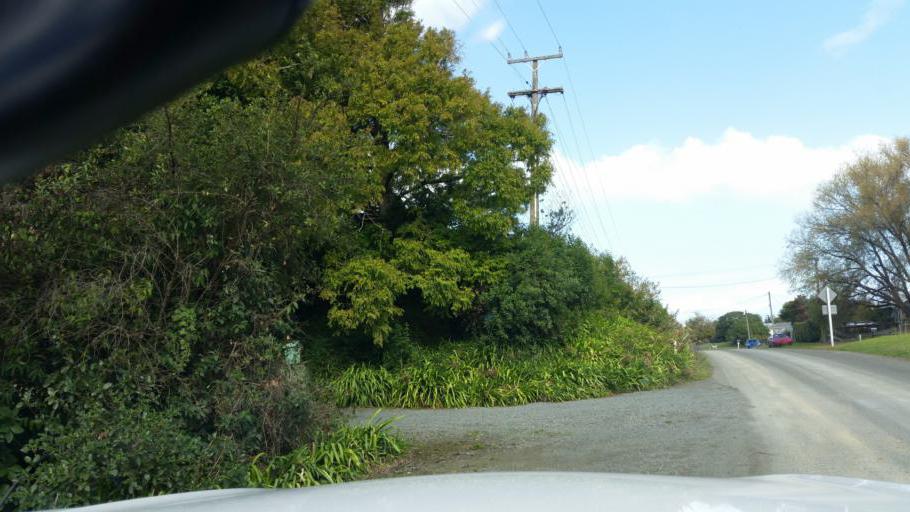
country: NZ
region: Northland
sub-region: Whangarei
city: Ruakaka
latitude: -36.1012
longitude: 174.3672
